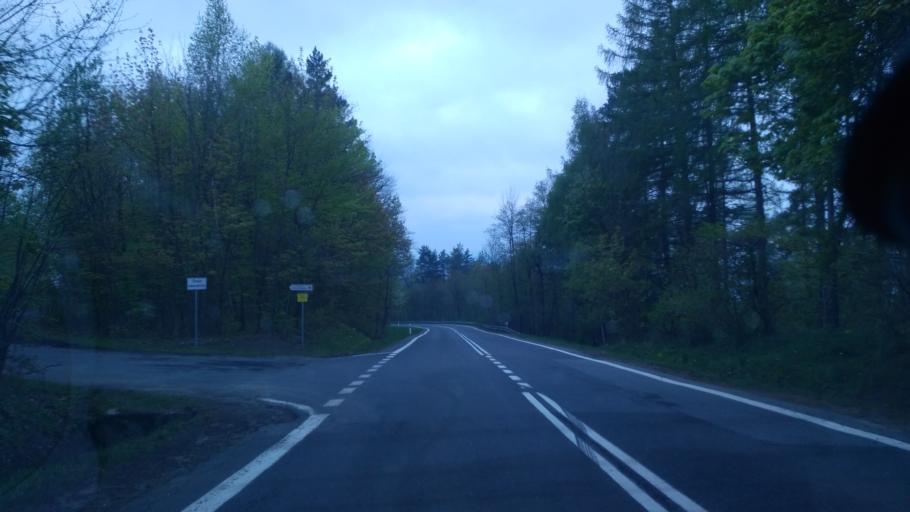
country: PL
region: Subcarpathian Voivodeship
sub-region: Powiat sanocki
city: Tyrawa Woloska
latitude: 49.5558
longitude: 22.3244
